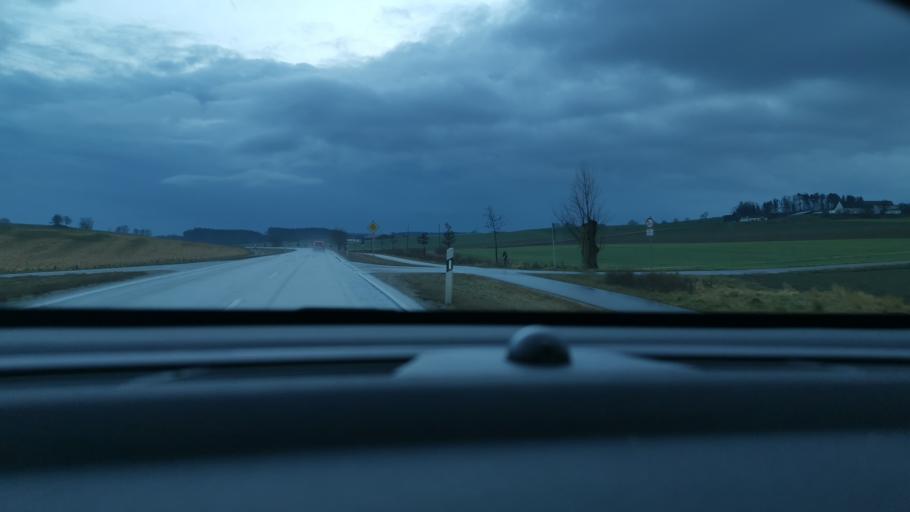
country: DE
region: Bavaria
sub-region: Swabia
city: Petersdorf
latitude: 48.5367
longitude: 11.0095
